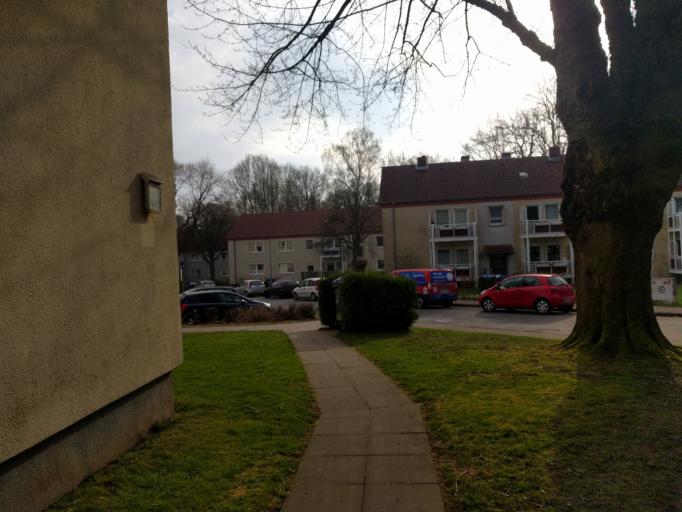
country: DE
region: North Rhine-Westphalia
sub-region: Regierungsbezirk Detmold
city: Bielefeld
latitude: 52.0420
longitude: 8.5094
